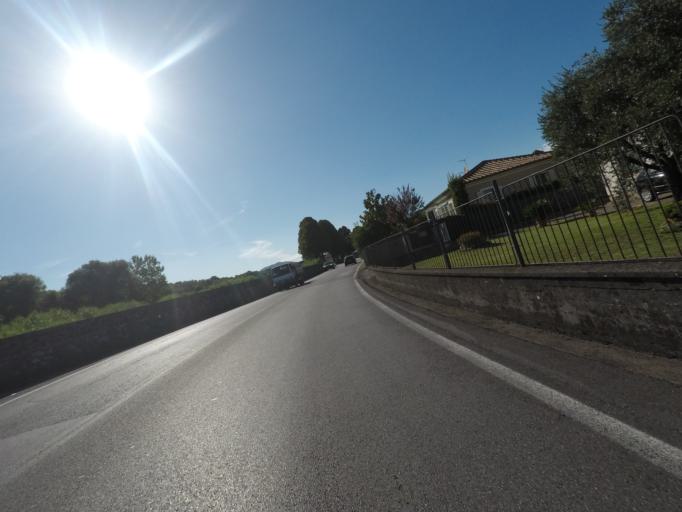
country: IT
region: Tuscany
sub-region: Provincia di Lucca
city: Lucca
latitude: 43.8702
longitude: 10.5042
